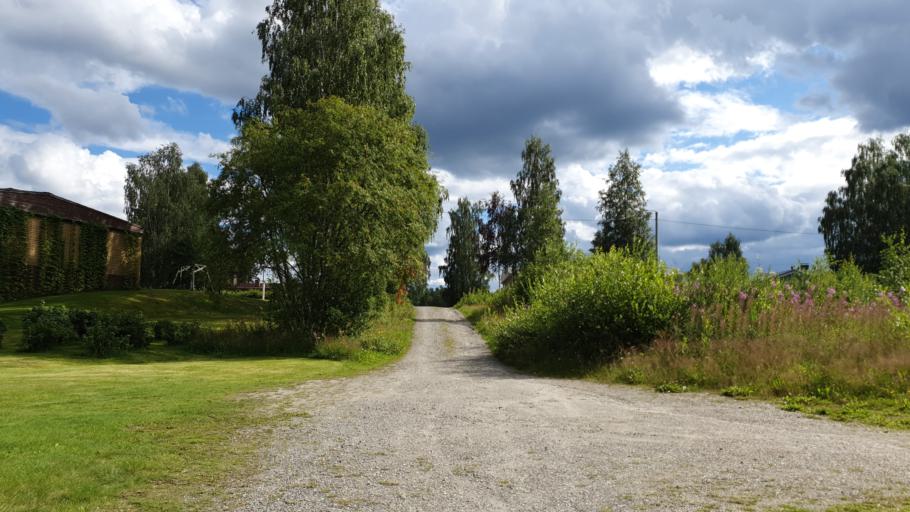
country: FI
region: Kainuu
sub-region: Kehys-Kainuu
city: Kuhmo
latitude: 64.1345
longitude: 29.5301
